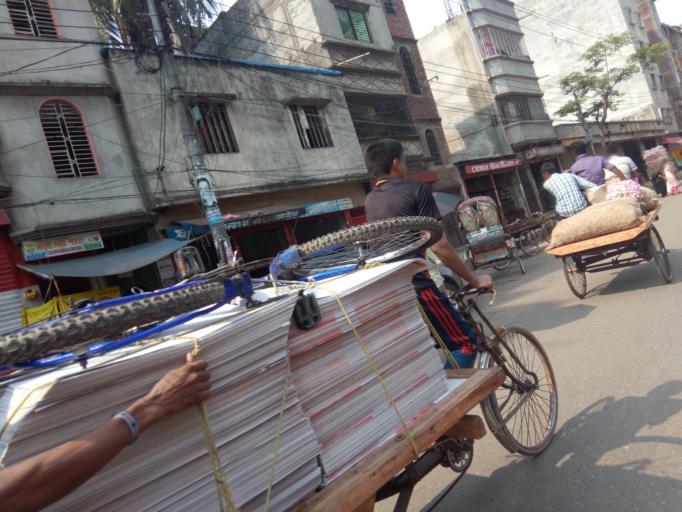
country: BD
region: Dhaka
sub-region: Dhaka
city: Dhaka
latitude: 23.7089
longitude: 90.4212
